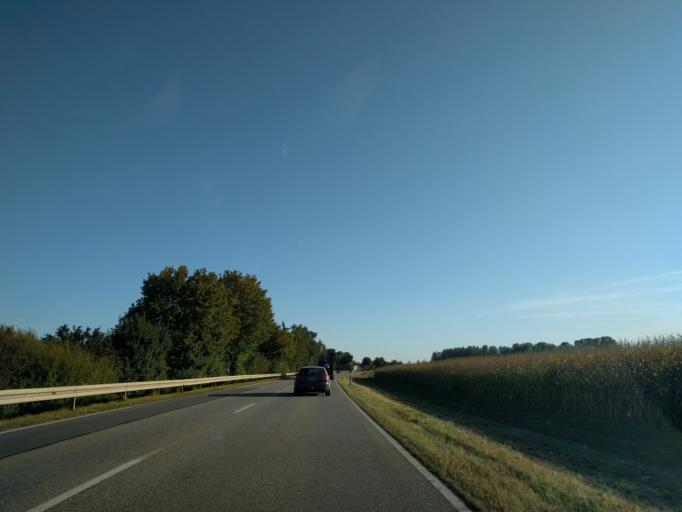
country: DE
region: Bavaria
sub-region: Lower Bavaria
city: Osterhofen
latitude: 48.7010
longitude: 13.0457
